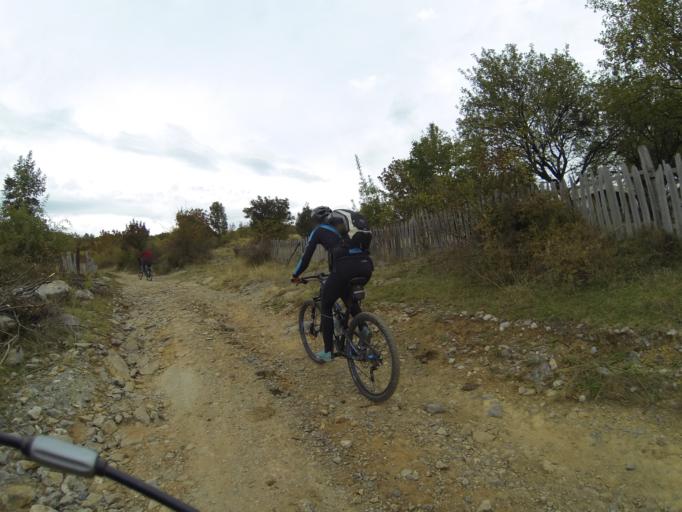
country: RO
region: Gorj
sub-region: Comuna Tismana
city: Sohodol
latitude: 45.0673
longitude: 22.8676
